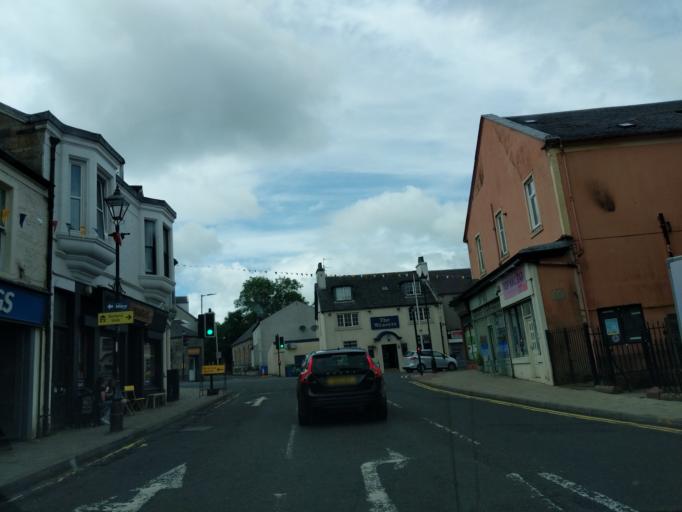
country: GB
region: Scotland
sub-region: South Lanarkshire
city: Strathaven
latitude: 55.6768
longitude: -4.0664
